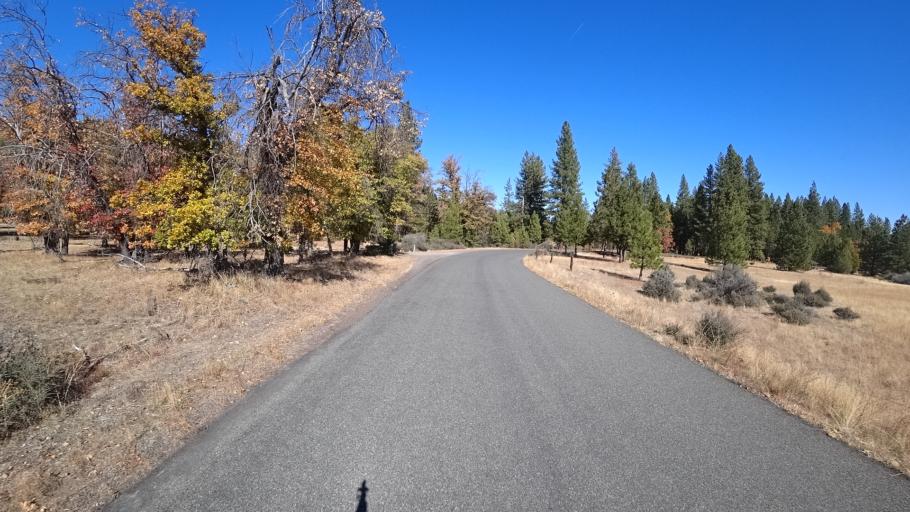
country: US
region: California
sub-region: Siskiyou County
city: Yreka
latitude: 41.5473
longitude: -122.9356
